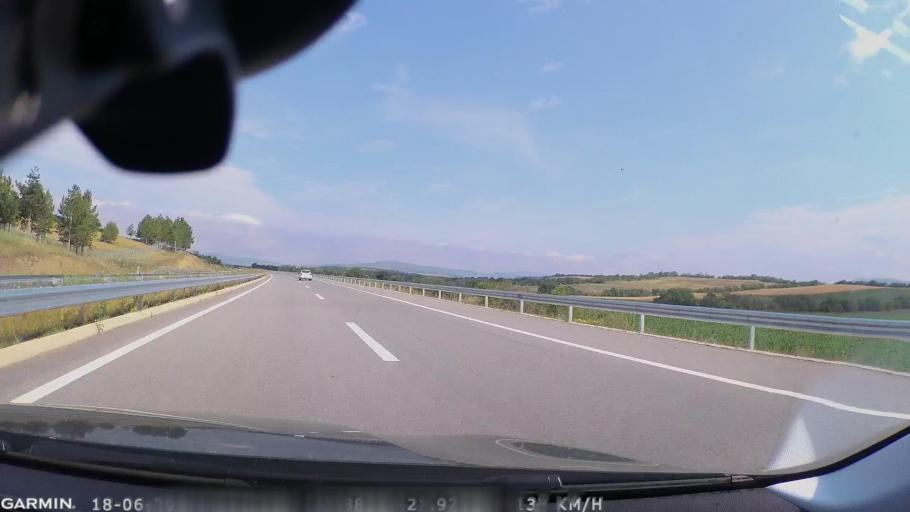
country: MK
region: Sveti Nikole
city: Sveti Nikole
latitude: 41.8905
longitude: 21.9290
